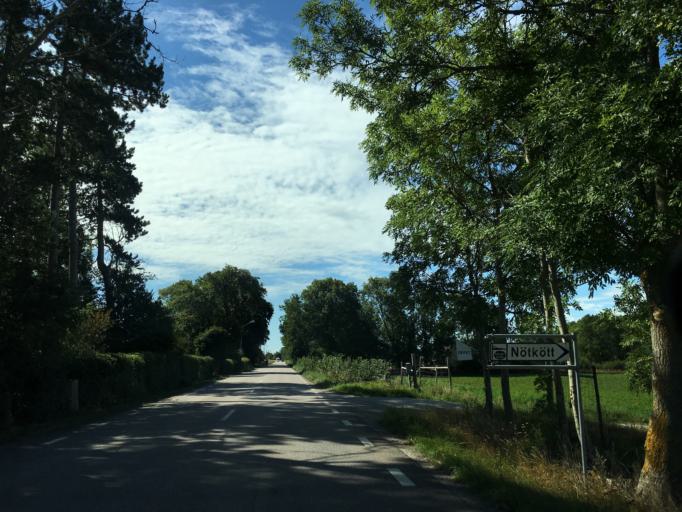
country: SE
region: Kalmar
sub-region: Morbylanga Kommun
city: Moerbylanga
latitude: 56.5146
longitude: 16.4387
